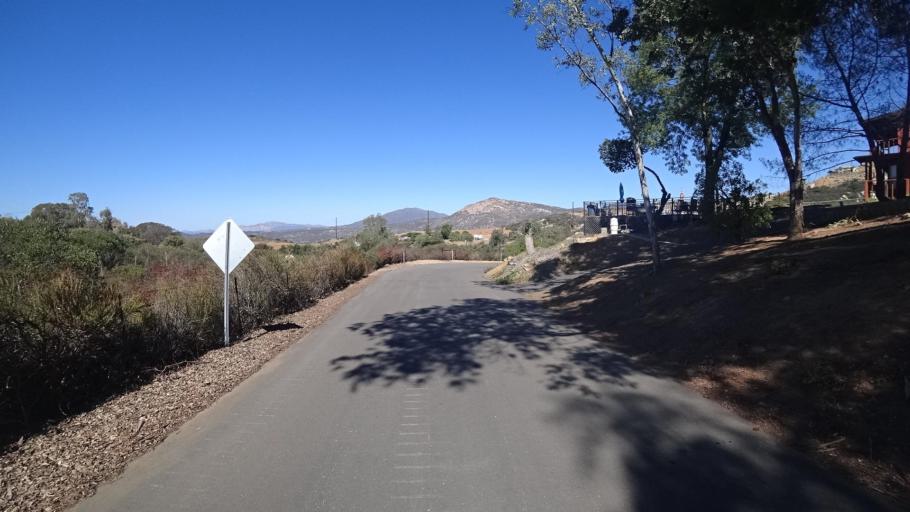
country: US
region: California
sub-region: San Diego County
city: Alpine
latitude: 32.7687
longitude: -116.7009
